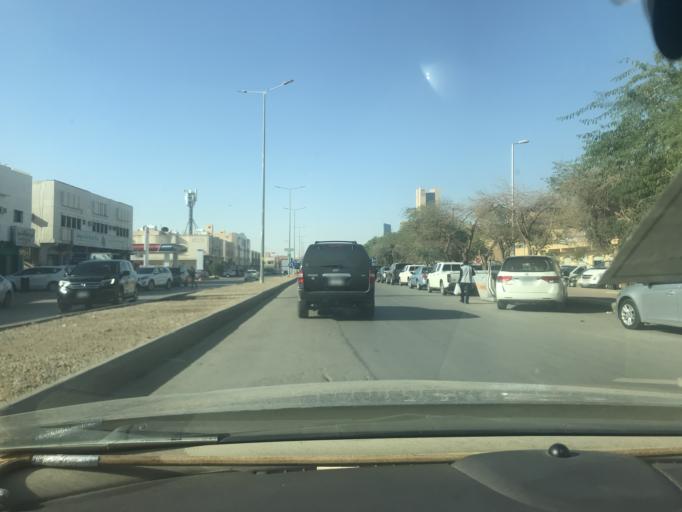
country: SA
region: Ar Riyad
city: Riyadh
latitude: 24.7531
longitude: 46.6679
